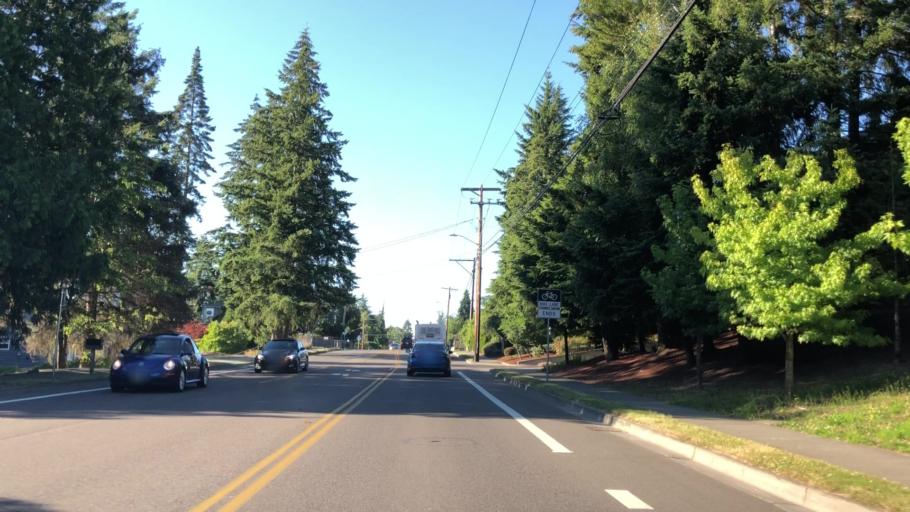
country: US
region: Washington
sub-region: Snohomish County
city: Mountlake Terrace
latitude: 47.7924
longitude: -122.2922
